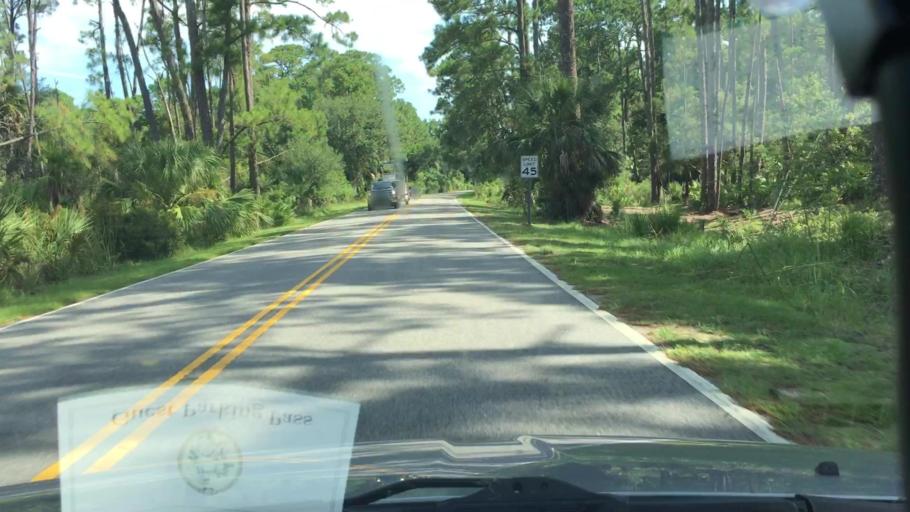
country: US
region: South Carolina
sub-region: Beaufort County
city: Beaufort
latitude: 32.3767
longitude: -80.4457
